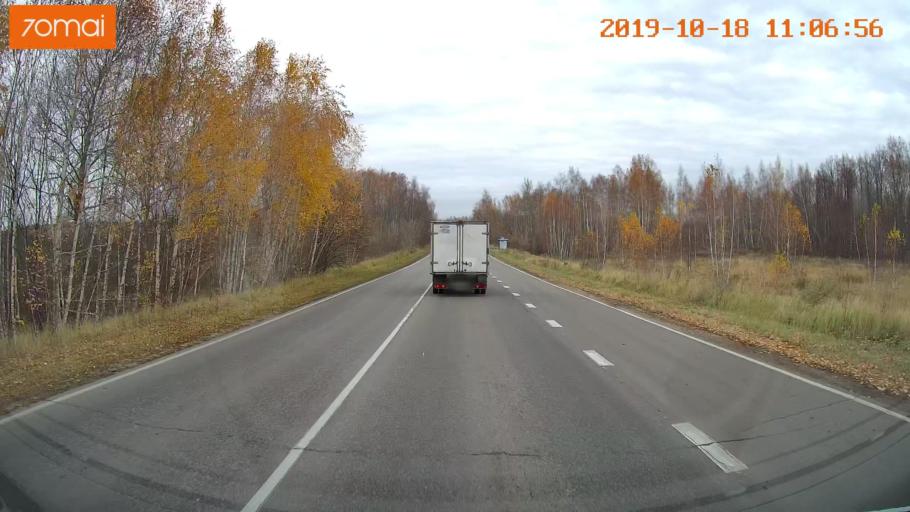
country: RU
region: Tula
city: Kimovsk
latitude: 53.9229
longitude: 38.5349
